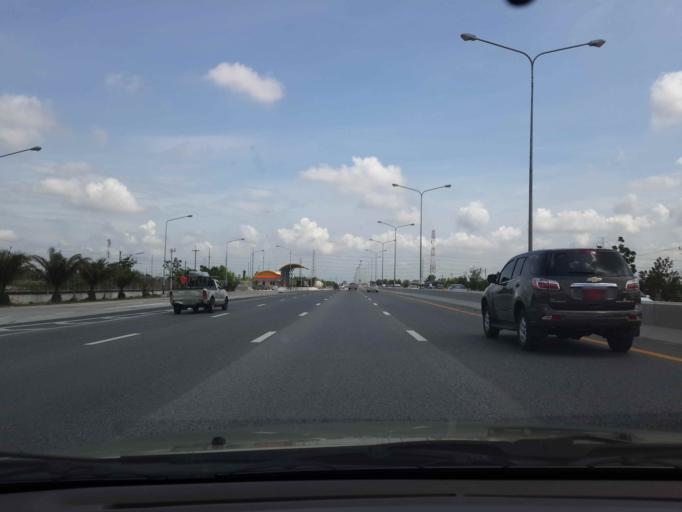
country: TH
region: Chachoengsao
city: Bang Pakong
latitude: 13.5029
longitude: 101.0394
